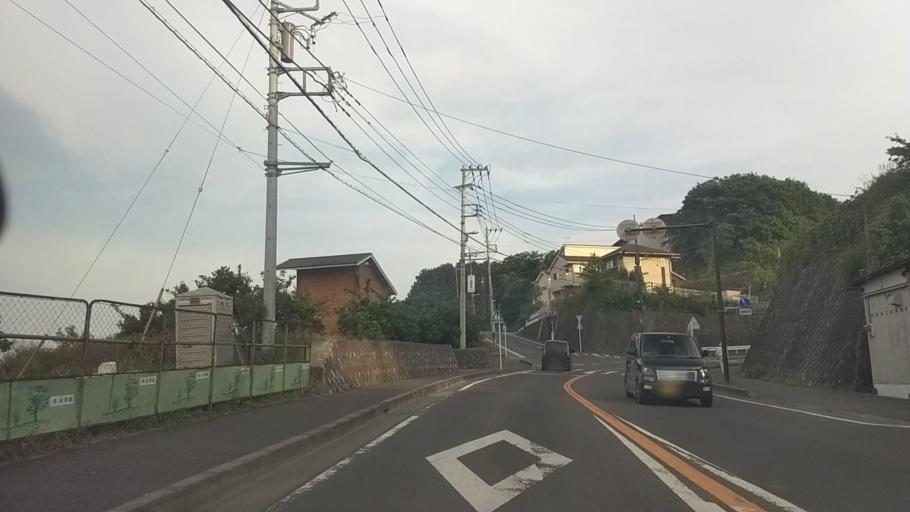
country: JP
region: Kanagawa
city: Odawara
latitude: 35.3269
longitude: 139.1071
